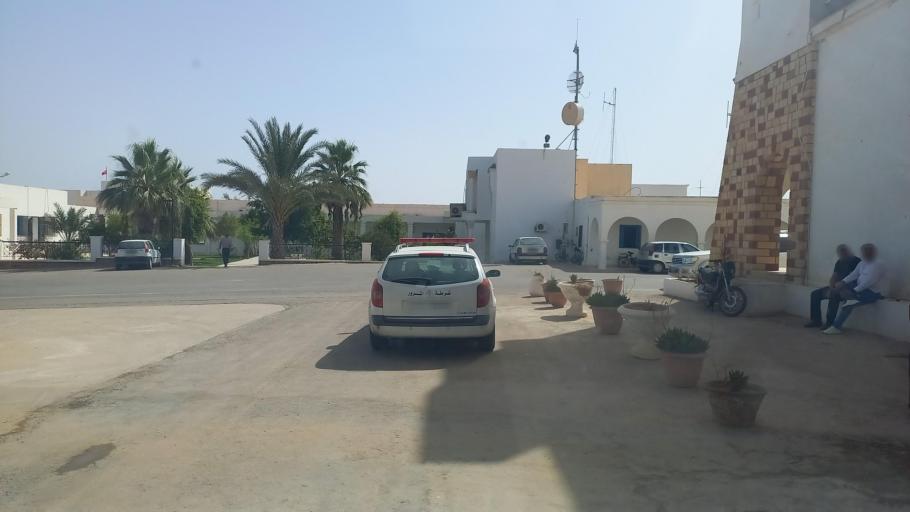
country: TN
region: Madanin
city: Medenine
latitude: 33.3424
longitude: 10.4924
